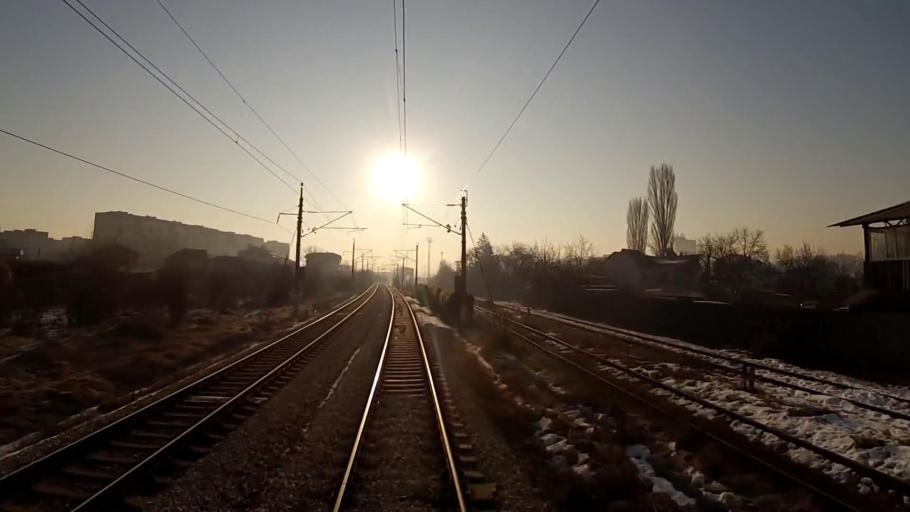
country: BG
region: Sofia-Capital
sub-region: Stolichna Obshtina
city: Sofia
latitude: 42.7312
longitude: 23.2750
